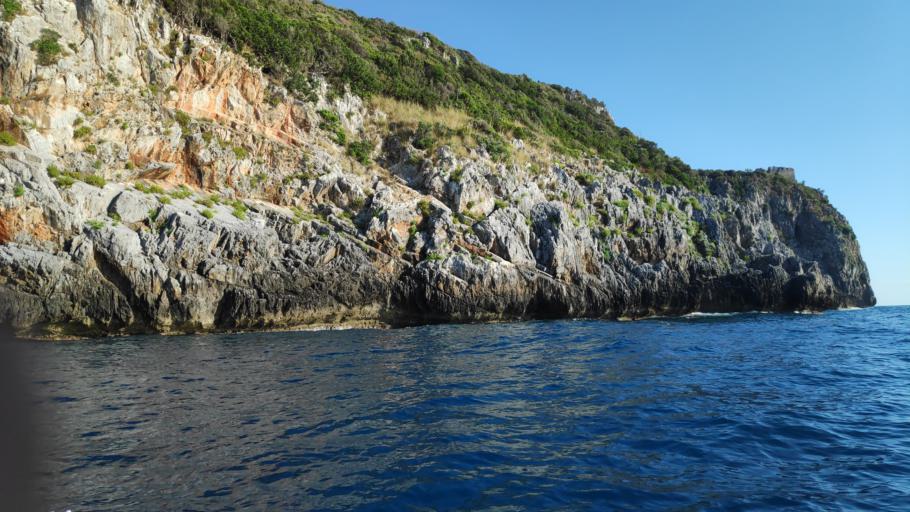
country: IT
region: Calabria
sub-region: Provincia di Cosenza
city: Praia a Mare
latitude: 39.8754
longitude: 15.7710
